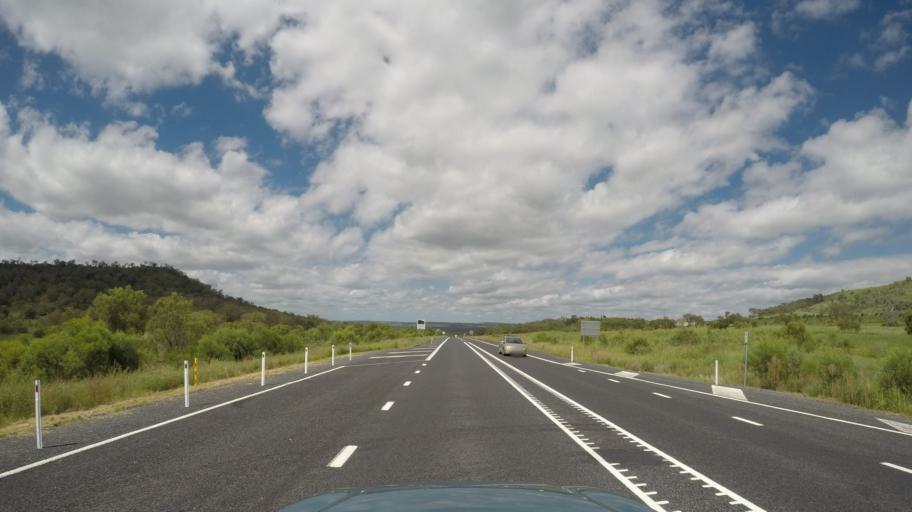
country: AU
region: Queensland
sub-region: Toowoomba
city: Westbrook
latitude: -27.5558
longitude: 151.8228
